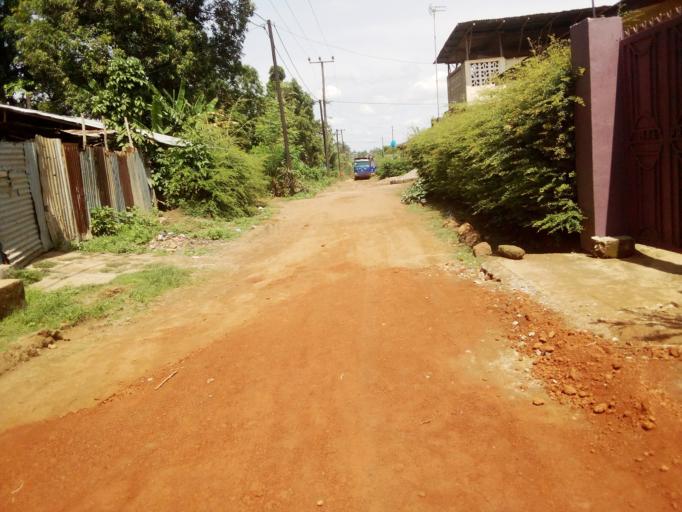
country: SL
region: Western Area
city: Waterloo
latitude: 8.3393
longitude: -13.0711
